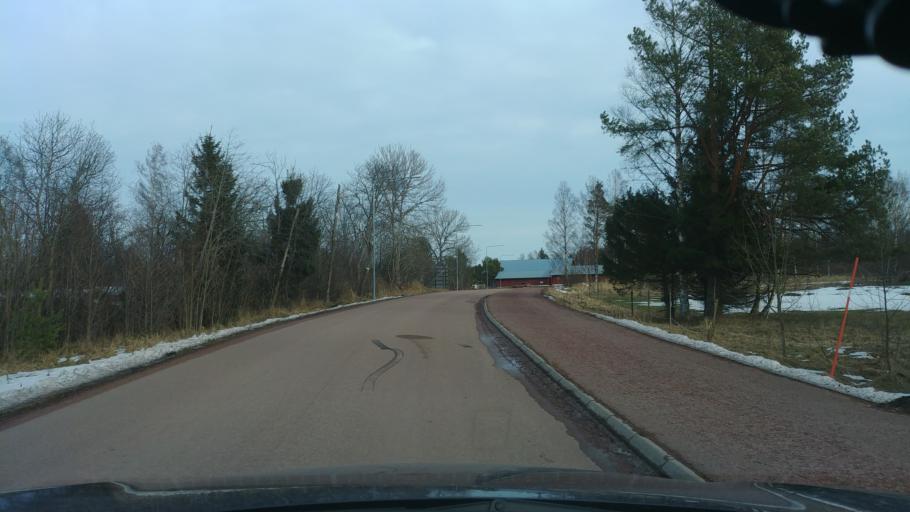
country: AX
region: Mariehamns stad
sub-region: Mariehamn
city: Mariehamn
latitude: 60.1052
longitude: 19.8967
